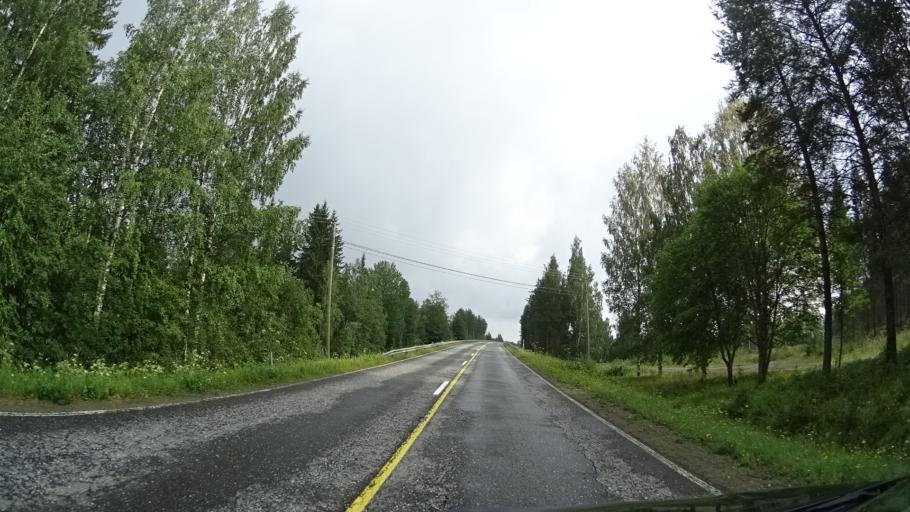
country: FI
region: North Karelia
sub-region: Keski-Karjala
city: Raeaekkylae
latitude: 62.3174
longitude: 29.5118
